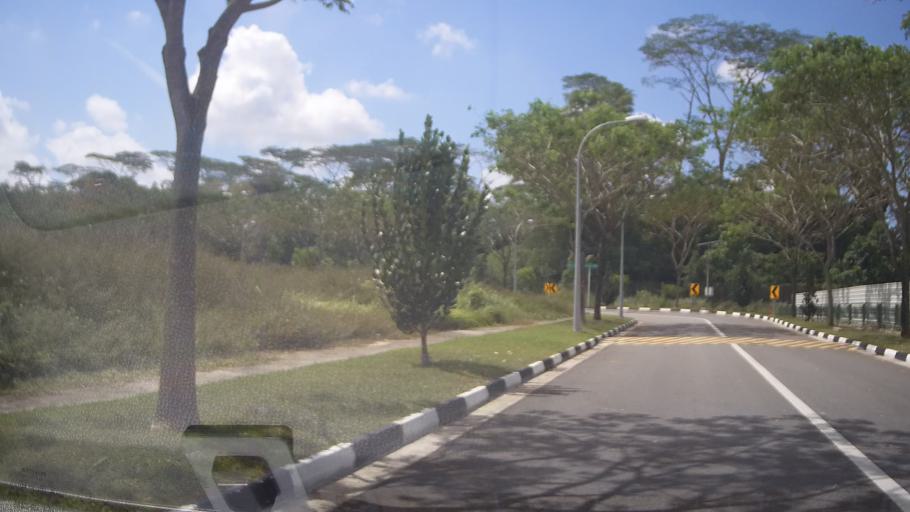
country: MY
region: Johor
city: Johor Bahru
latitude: 1.4193
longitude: 103.7220
